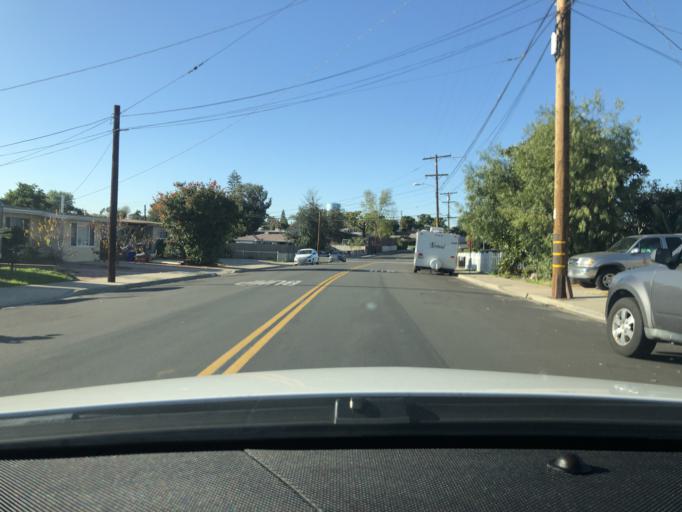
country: US
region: California
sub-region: San Diego County
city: Lemon Grove
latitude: 32.7453
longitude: -117.0615
